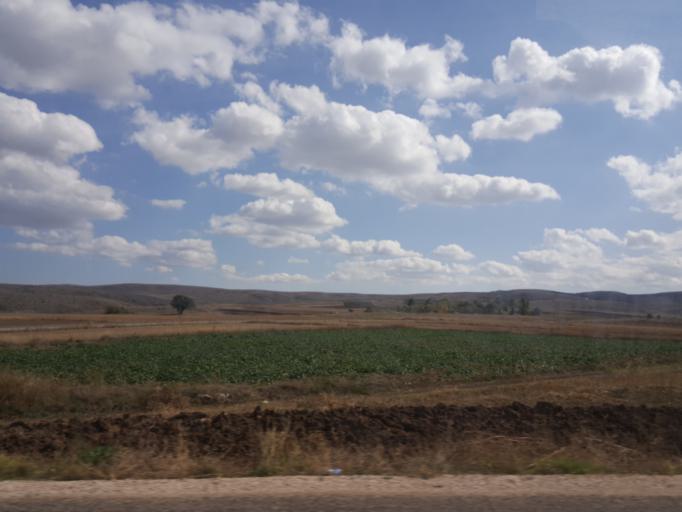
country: TR
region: Tokat
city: Artova
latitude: 40.1522
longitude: 36.3929
